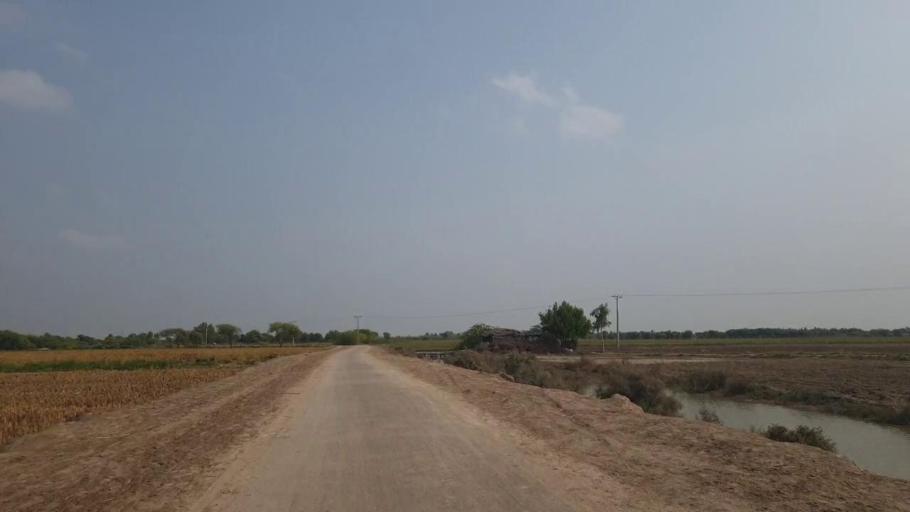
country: PK
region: Sindh
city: Badin
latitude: 24.5474
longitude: 68.7208
